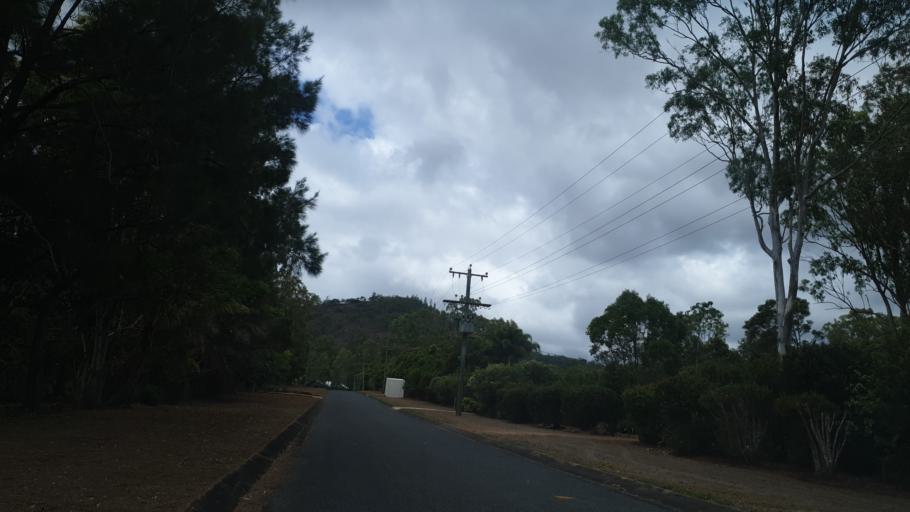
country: AU
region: Queensland
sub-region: Tablelands
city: Tolga
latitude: -17.2088
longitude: 145.4393
